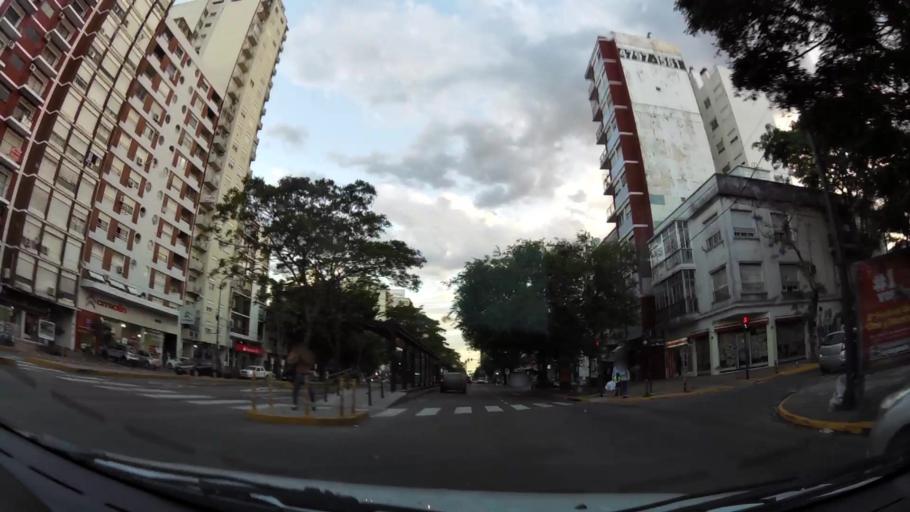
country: AR
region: Buenos Aires
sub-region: Partido de Vicente Lopez
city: Olivos
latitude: -34.5250
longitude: -58.4833
